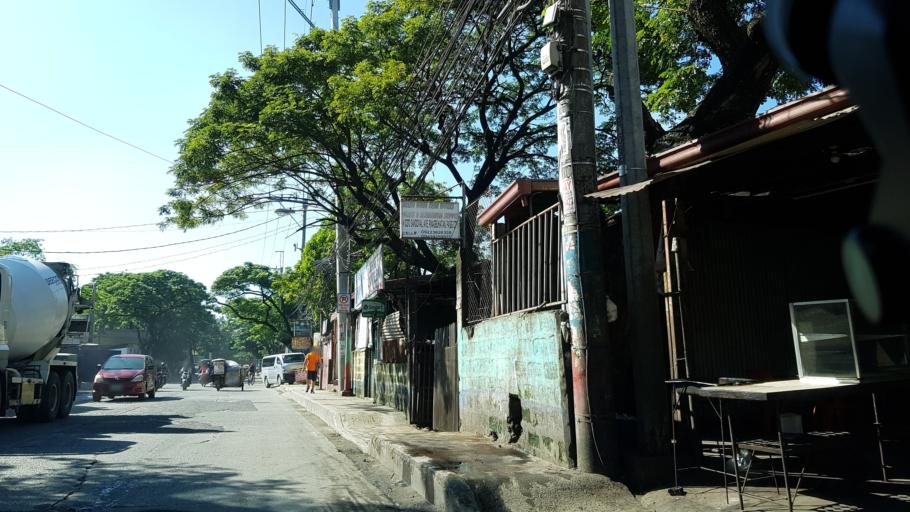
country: PH
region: Calabarzon
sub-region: Province of Rizal
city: Pateros
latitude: 14.5581
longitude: 121.0965
